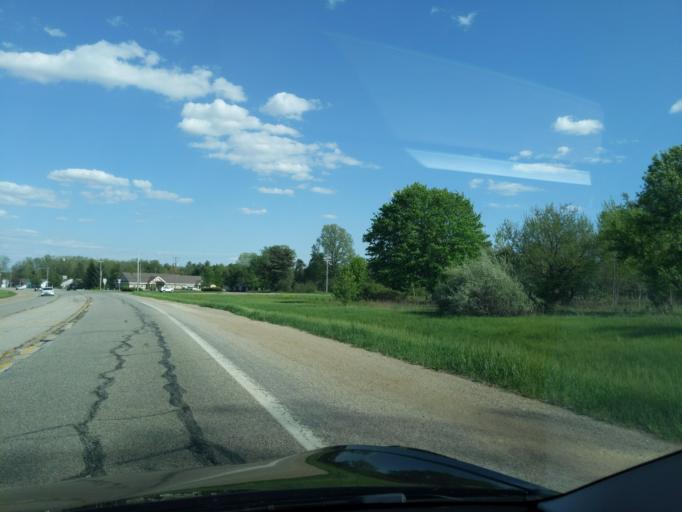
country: US
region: Michigan
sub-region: Eaton County
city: Grand Ledge
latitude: 42.7420
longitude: -84.7566
